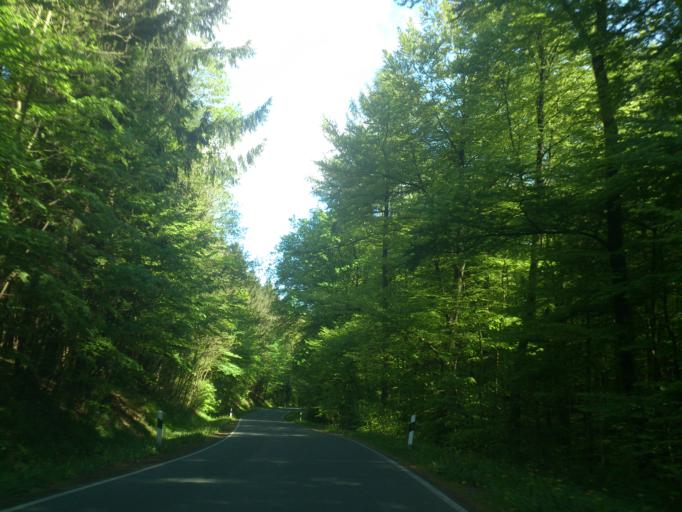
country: DE
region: North Rhine-Westphalia
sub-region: Regierungsbezirk Detmold
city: Willebadessen
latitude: 51.6550
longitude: 9.0369
